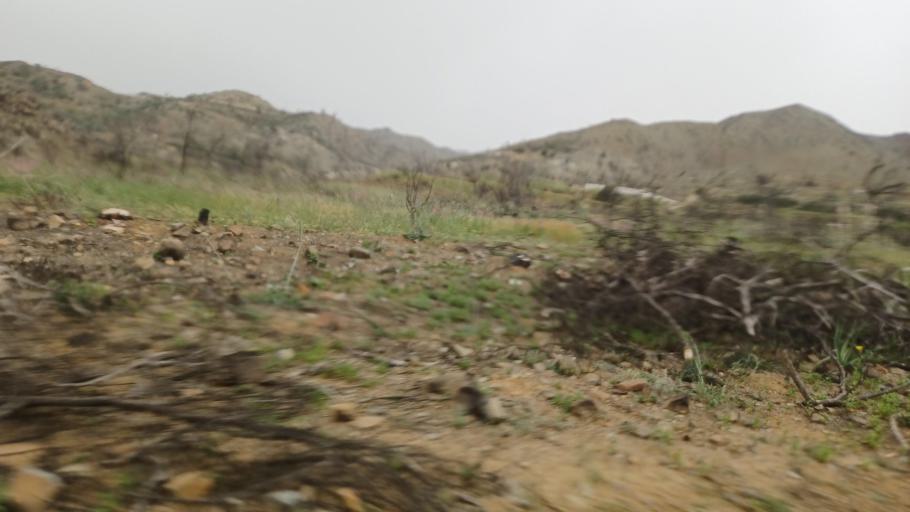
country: CY
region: Limassol
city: Parekklisha
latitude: 34.8488
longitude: 33.1418
